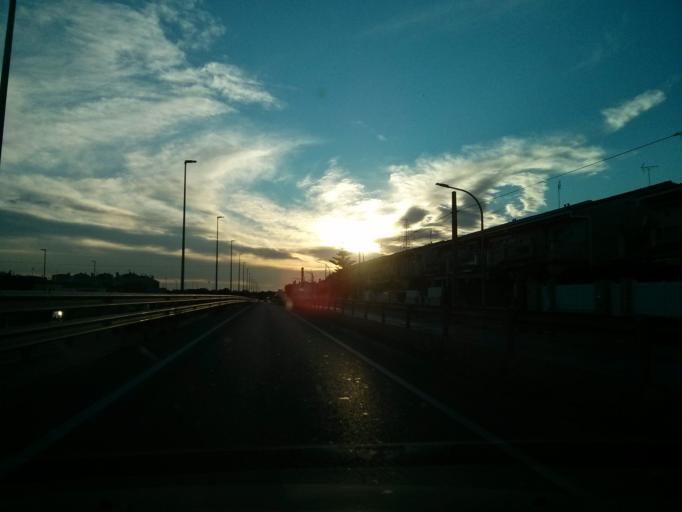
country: ES
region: Catalonia
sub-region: Provincia de Tarragona
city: El Vendrell
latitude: 41.1910
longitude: 1.5217
